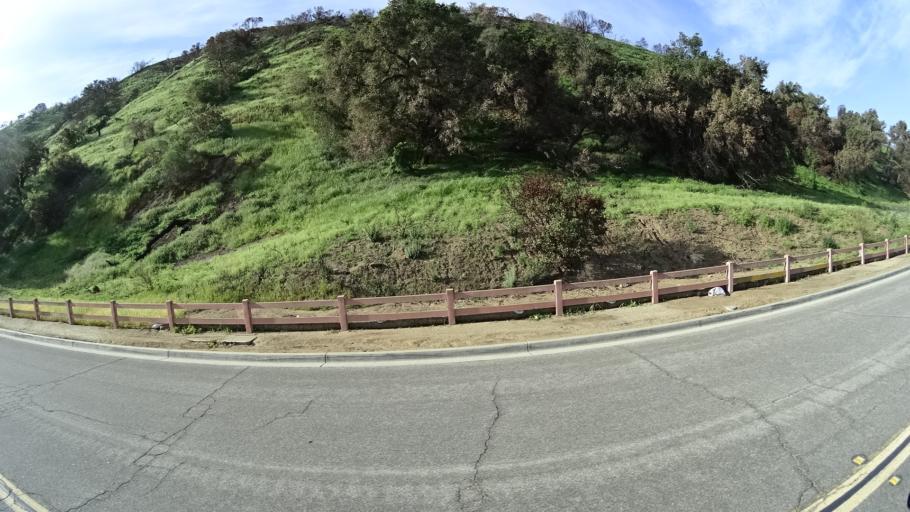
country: US
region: California
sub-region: Ventura County
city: Thousand Oaks
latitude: 34.2121
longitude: -118.8180
